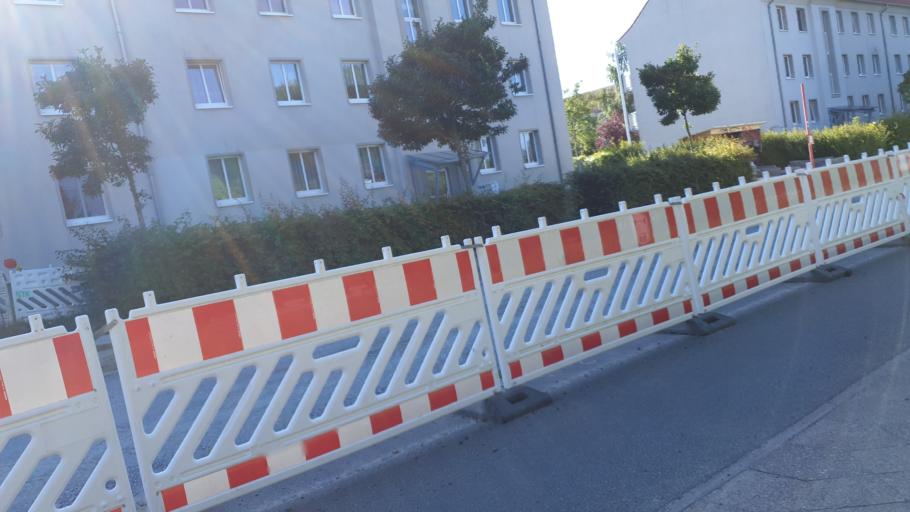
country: DE
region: Mecklenburg-Vorpommern
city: Stralsund
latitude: 54.3327
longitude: 13.0770
